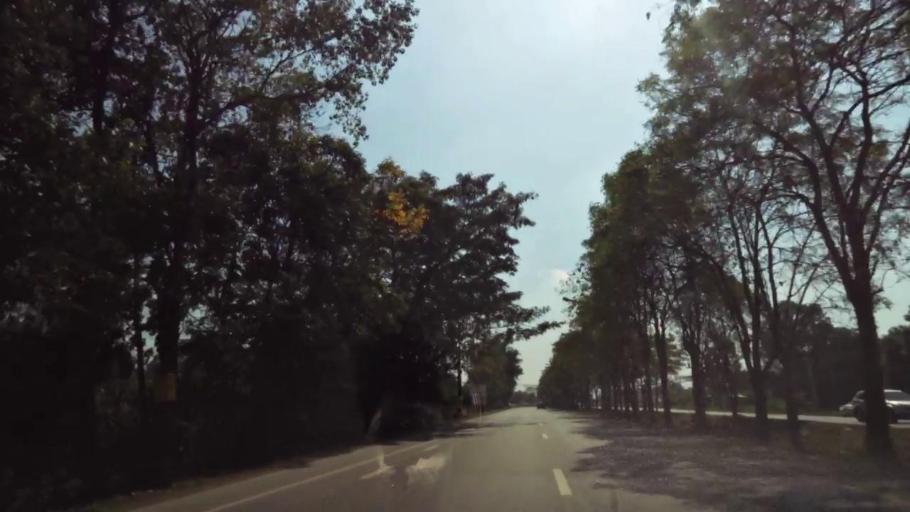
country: TH
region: Phichit
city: Bueng Na Rang
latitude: 16.1923
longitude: 100.1286
